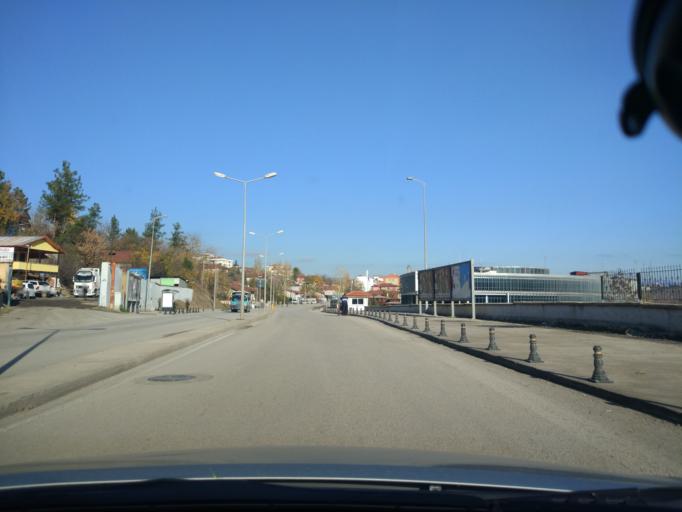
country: TR
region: Karabuk
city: Karabuk
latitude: 41.2048
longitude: 32.6324
